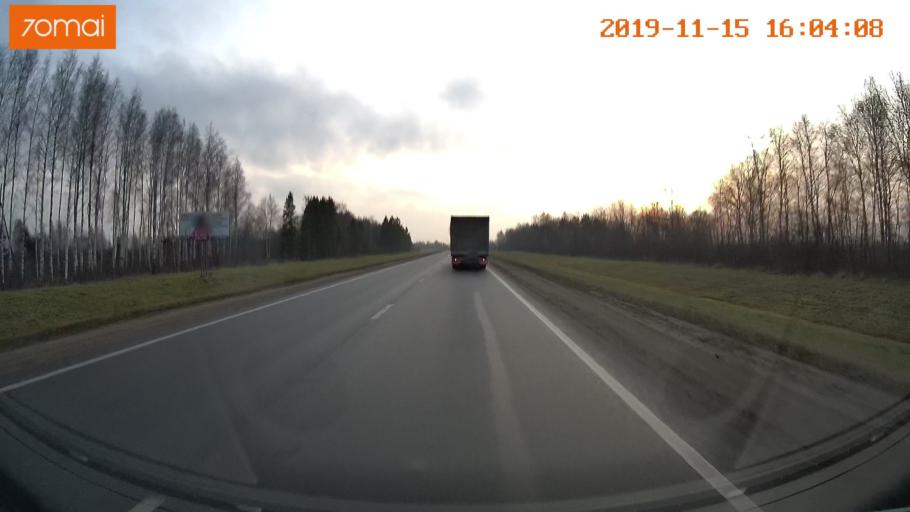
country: RU
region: Jaroslavl
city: Yaroslavl
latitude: 57.7511
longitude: 39.9056
